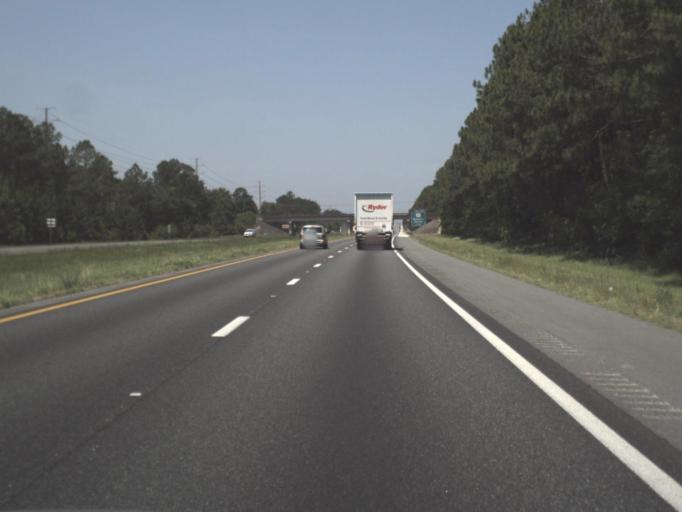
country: US
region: Florida
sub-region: Duval County
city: Baldwin
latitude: 30.2906
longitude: -81.9626
